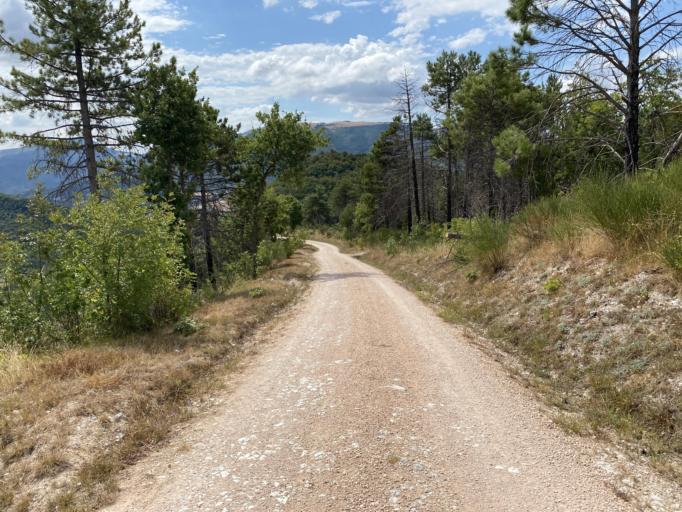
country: IT
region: The Marches
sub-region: Provincia di Pesaro e Urbino
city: Canavaccio
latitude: 43.7075
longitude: 12.7149
